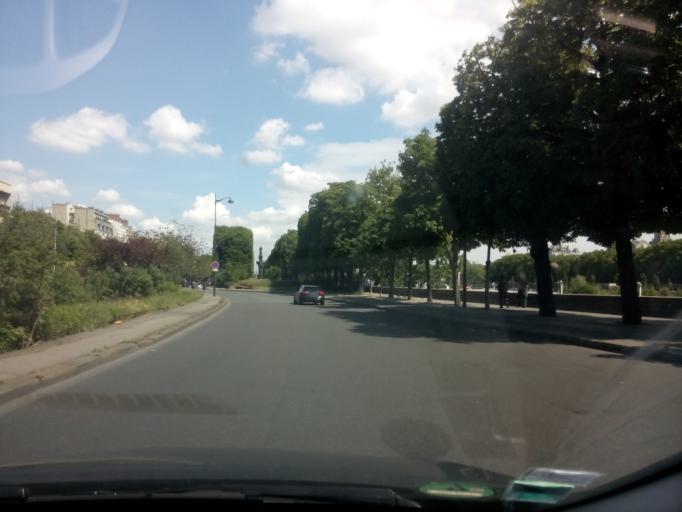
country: FR
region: Ile-de-France
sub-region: Departement des Hauts-de-Seine
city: Levallois-Perret
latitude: 48.8642
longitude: 2.3024
